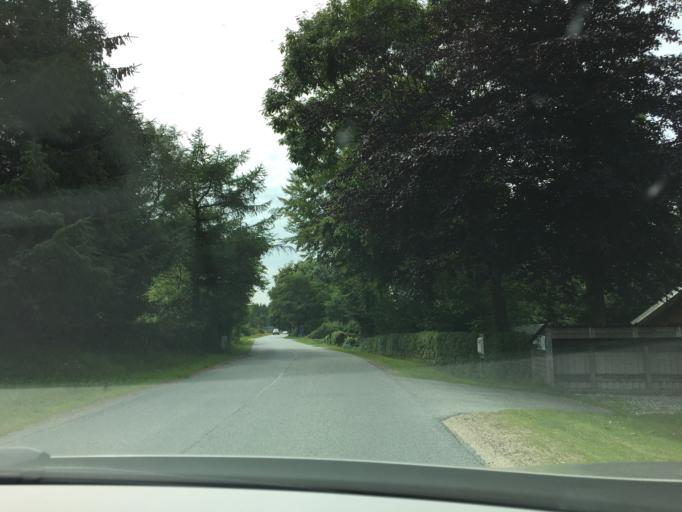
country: DK
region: South Denmark
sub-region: Varde Kommune
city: Oksbol
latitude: 55.7604
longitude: 8.2523
